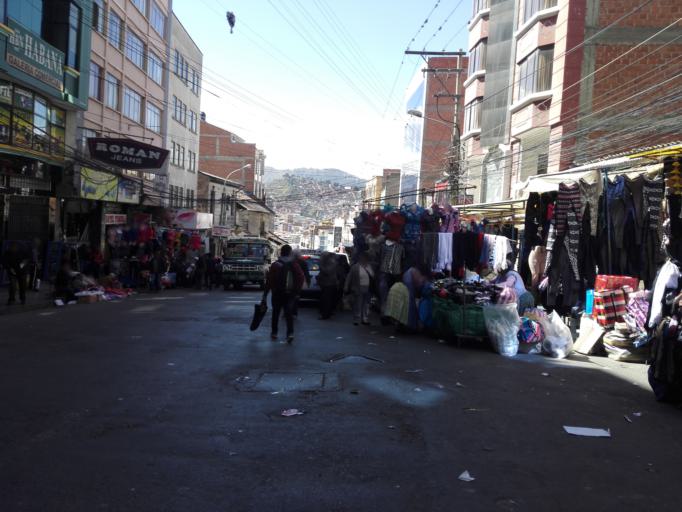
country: BO
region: La Paz
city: La Paz
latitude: -16.4951
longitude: -68.1432
